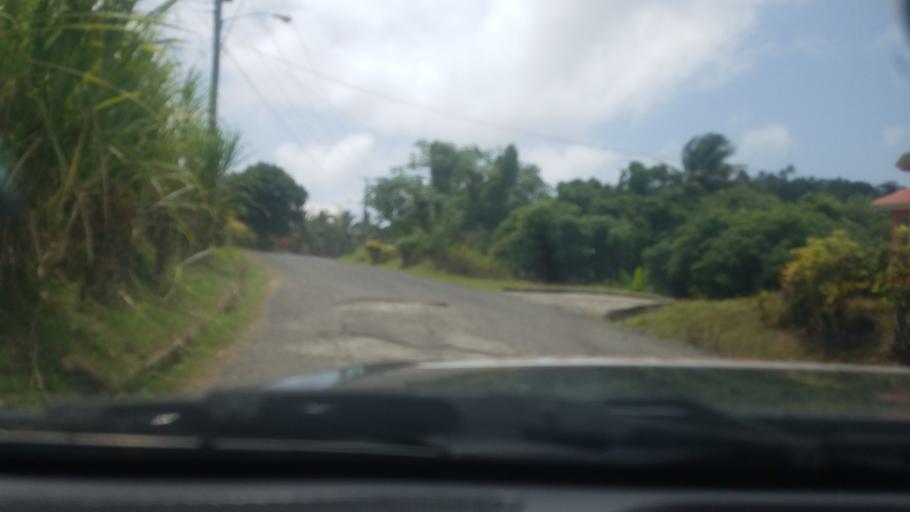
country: LC
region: Laborie Quarter
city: Laborie
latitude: 13.7907
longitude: -60.9528
